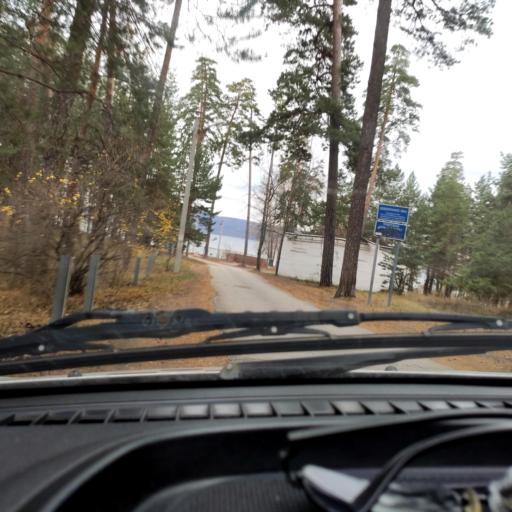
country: RU
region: Samara
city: Tol'yatti
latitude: 53.4749
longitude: 49.3338
